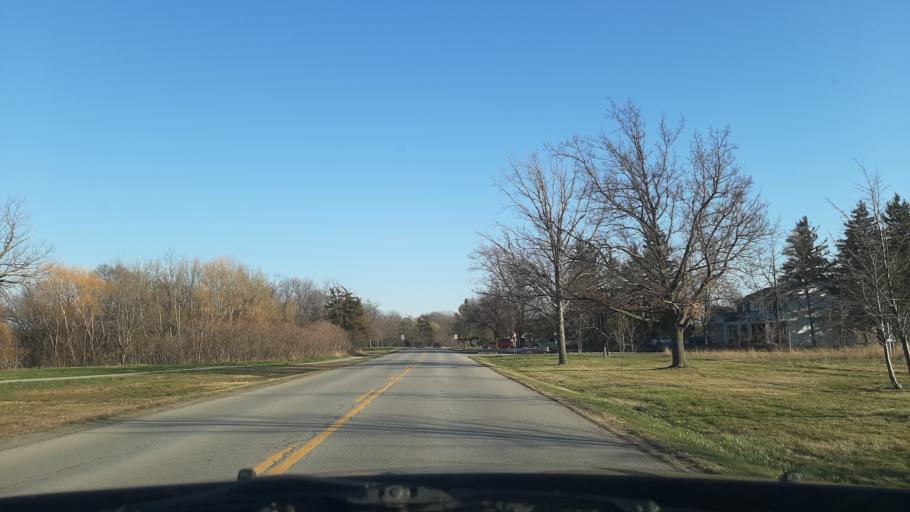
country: US
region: New York
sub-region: Niagara County
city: Lewiston
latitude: 43.2050
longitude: -79.0583
